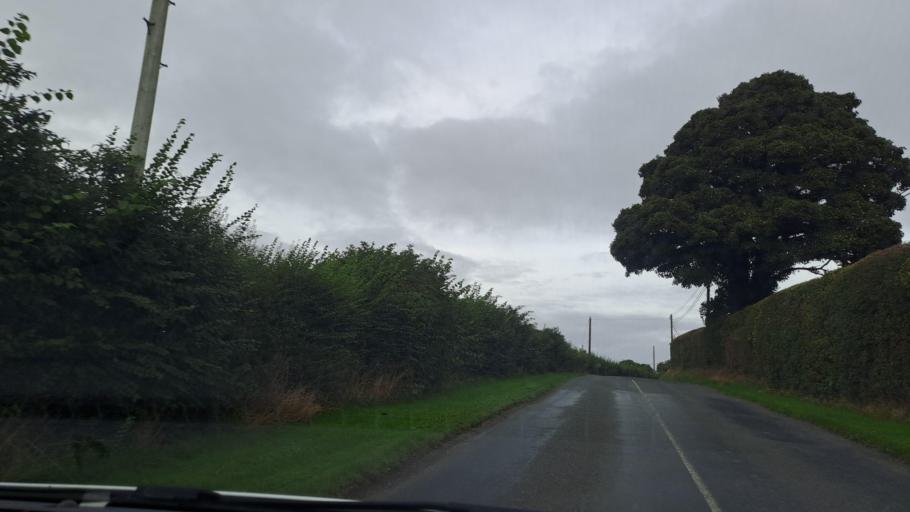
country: IE
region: Leinster
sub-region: Lu
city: Ardee
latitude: 53.8491
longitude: -6.6374
